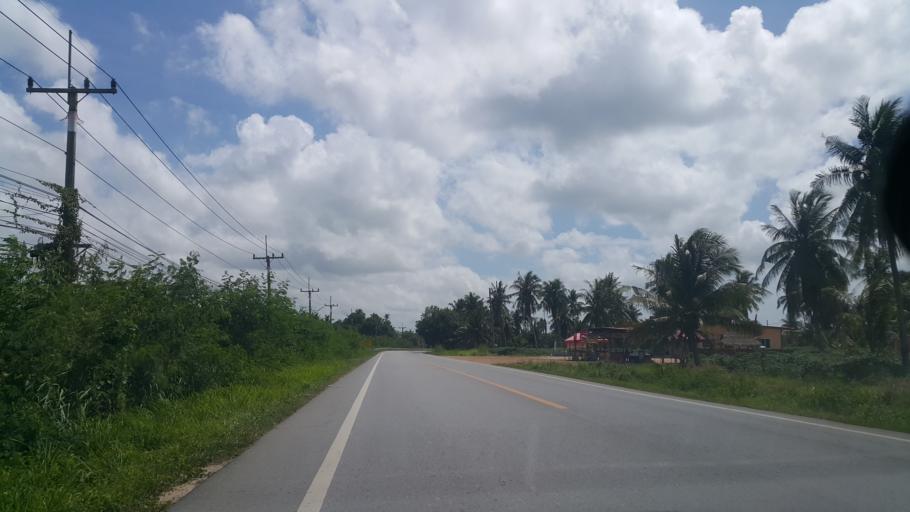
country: TH
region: Rayong
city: Ban Chang
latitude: 12.7926
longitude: 101.0353
